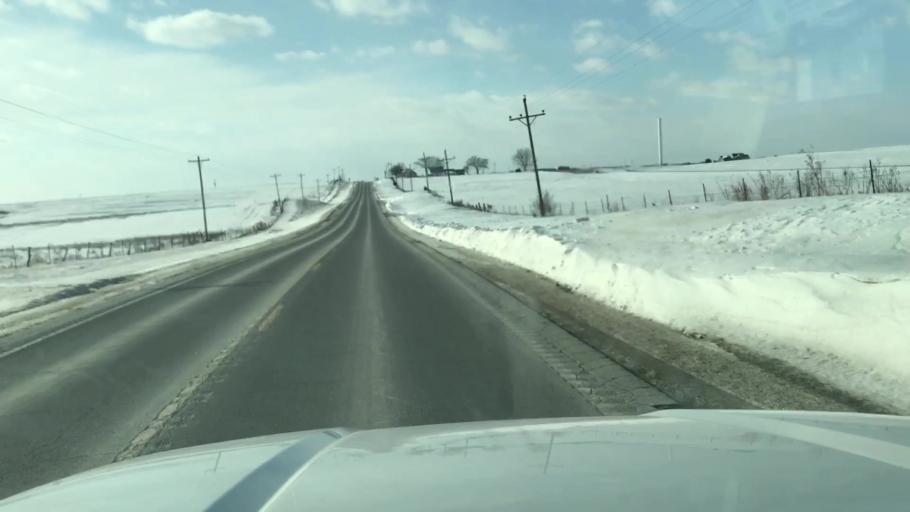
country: US
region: Missouri
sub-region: Nodaway County
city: Maryville
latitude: 40.3442
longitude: -94.7524
